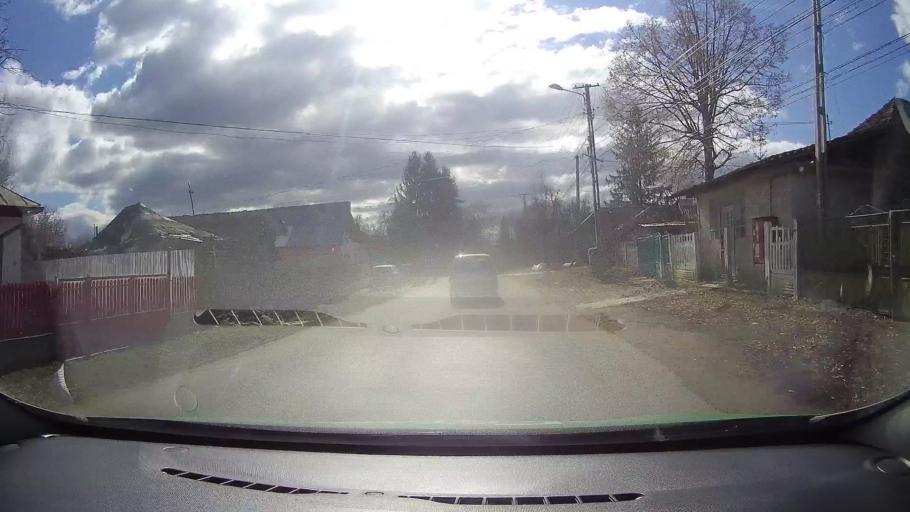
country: RO
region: Dambovita
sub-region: Oras Pucioasa
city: Pucioasa
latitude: 45.0619
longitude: 25.4251
